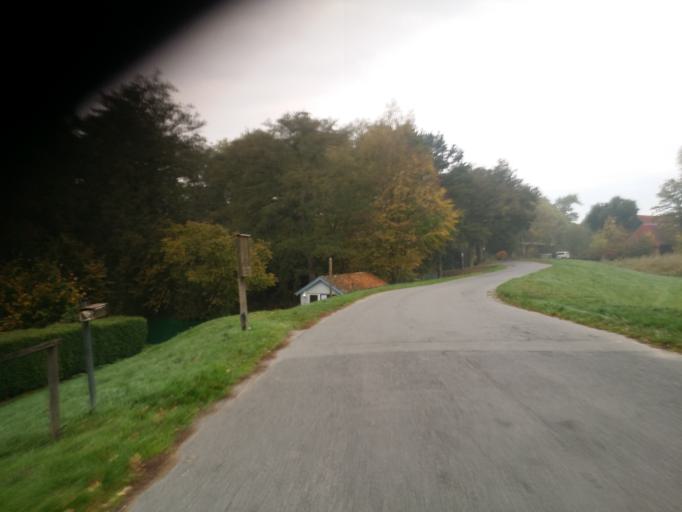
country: DE
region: Lower Saxony
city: Lilienthal
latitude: 53.1434
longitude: 8.8461
